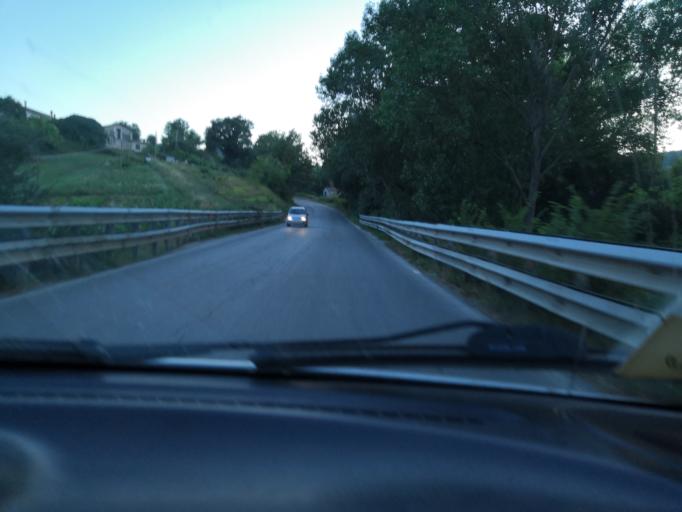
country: IT
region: Molise
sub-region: Provincia di Campobasso
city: Jelsi
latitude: 41.5136
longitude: 14.7914
